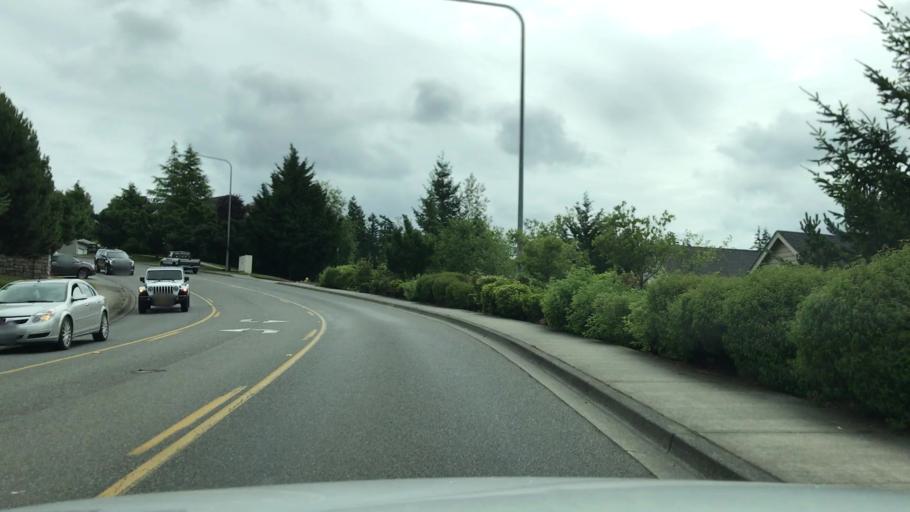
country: US
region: Washington
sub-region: King County
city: Issaquah
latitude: 47.5482
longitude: -122.0315
